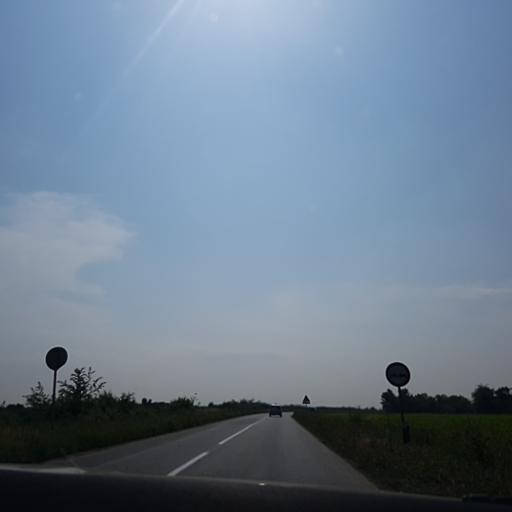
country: RS
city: Neuzina
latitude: 45.3415
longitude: 20.7181
